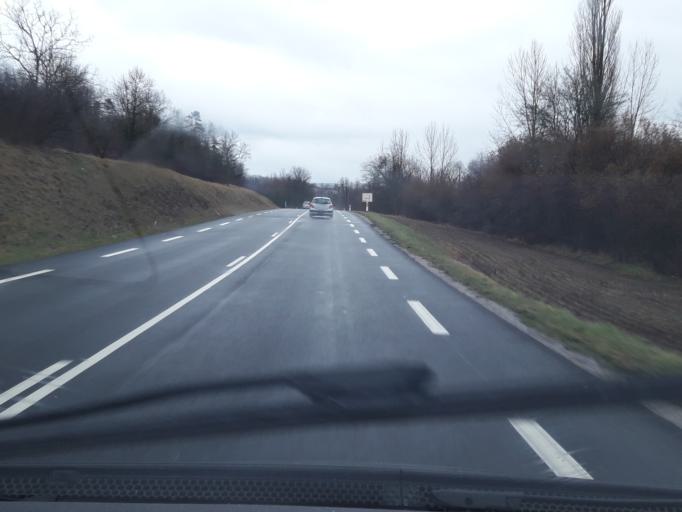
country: FR
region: Rhone-Alpes
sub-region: Departement de l'Ain
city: Belley
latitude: 45.7857
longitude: 5.6858
